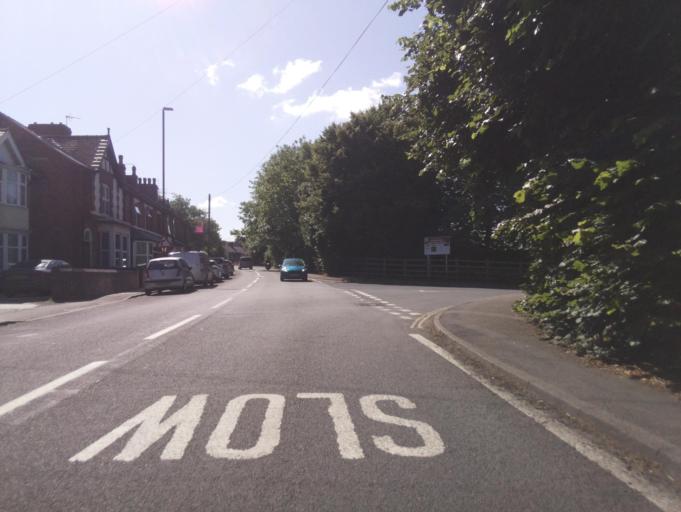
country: GB
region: England
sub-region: Derbyshire
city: Belper
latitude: 53.0176
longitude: -1.4845
